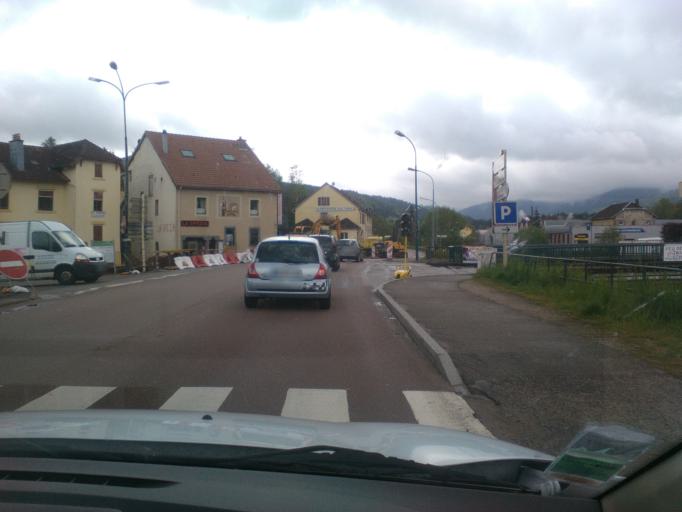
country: FR
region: Lorraine
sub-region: Departement des Vosges
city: Vagney
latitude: 47.9939
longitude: 6.7160
